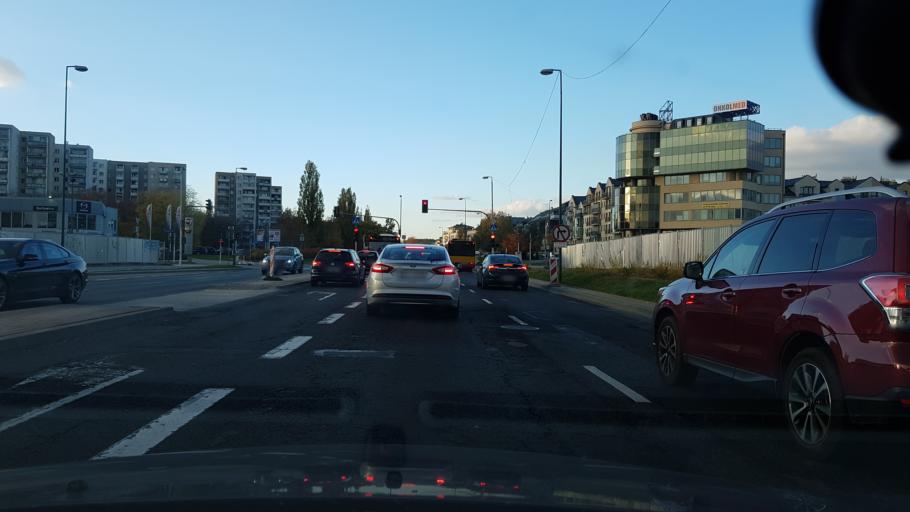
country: PL
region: Masovian Voivodeship
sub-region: Warszawa
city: Ursynow
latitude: 52.1488
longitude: 21.0603
